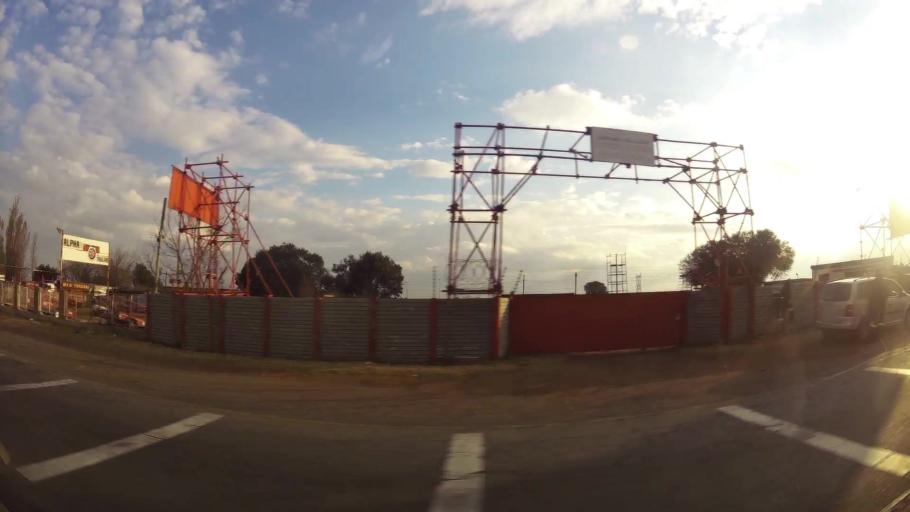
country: ZA
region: Gauteng
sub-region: Sedibeng District Municipality
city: Vanderbijlpark
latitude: -26.6987
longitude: 27.8089
